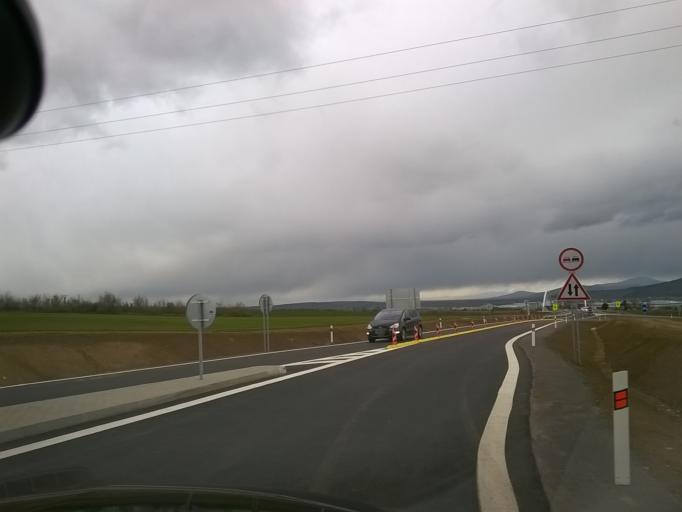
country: SK
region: Nitriansky
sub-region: Okres Nitra
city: Nitra
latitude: 48.3139
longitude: 18.0073
